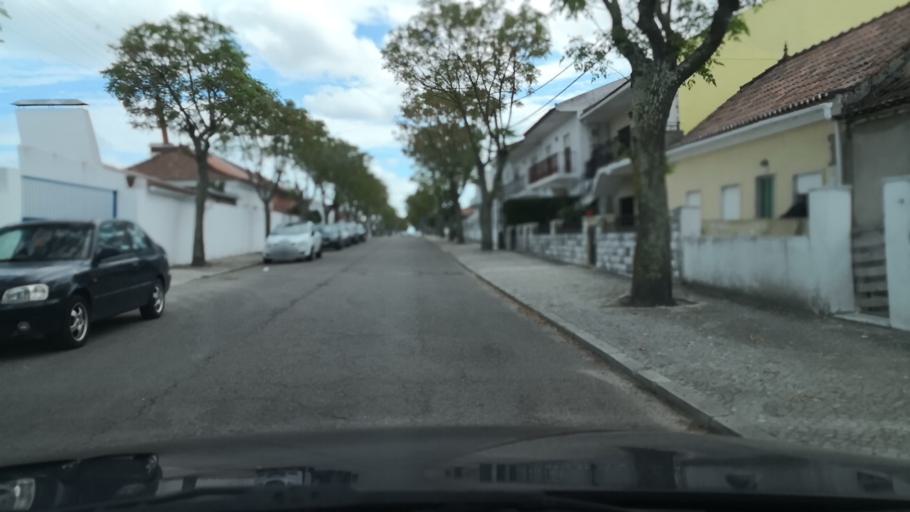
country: PT
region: Evora
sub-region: Vendas Novas
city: Vendas Novas
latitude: 38.6794
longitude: -8.4695
